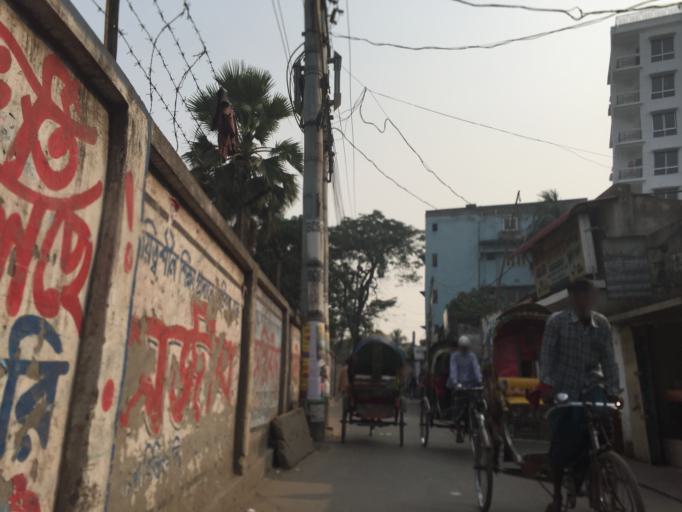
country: BD
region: Dhaka
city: Azimpur
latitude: 23.7305
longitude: 90.3812
